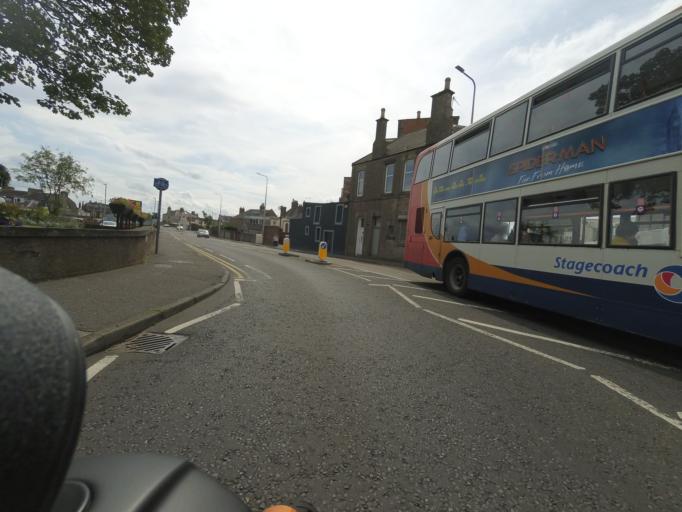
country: GB
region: Scotland
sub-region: Fife
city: Leven
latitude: 56.1962
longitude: -2.9959
